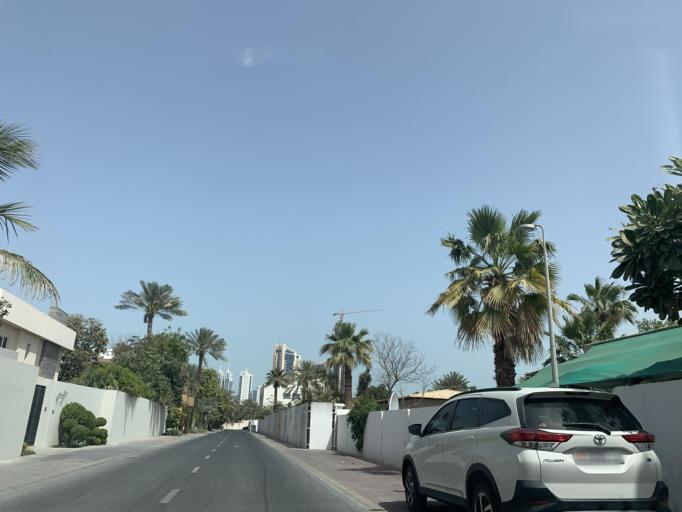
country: BH
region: Manama
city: Jidd Hafs
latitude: 26.2187
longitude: 50.5608
